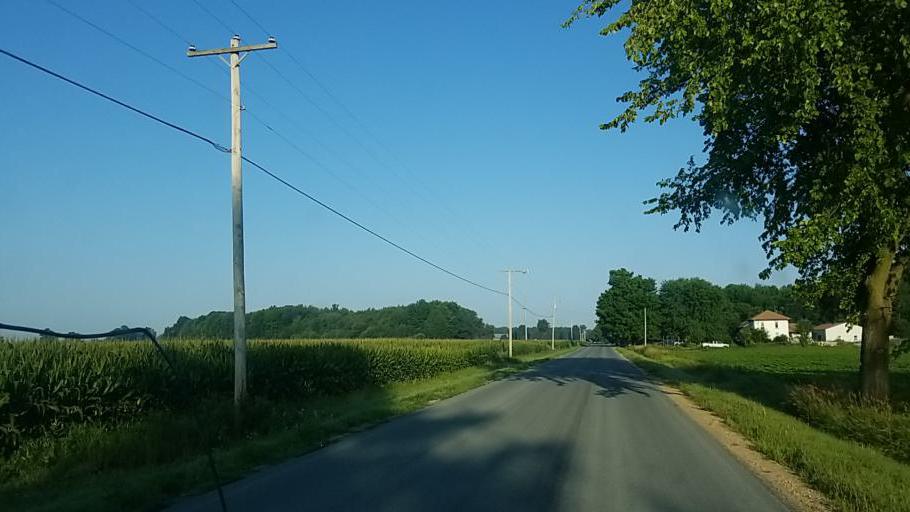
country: US
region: Michigan
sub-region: Montcalm County
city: Howard City
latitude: 43.3666
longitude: -85.4367
